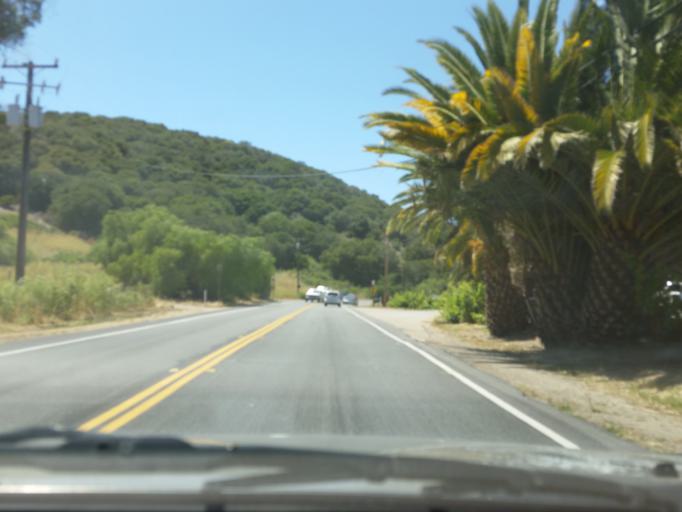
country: US
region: California
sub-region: San Luis Obispo County
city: Avila Beach
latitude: 35.1822
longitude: -120.7061
